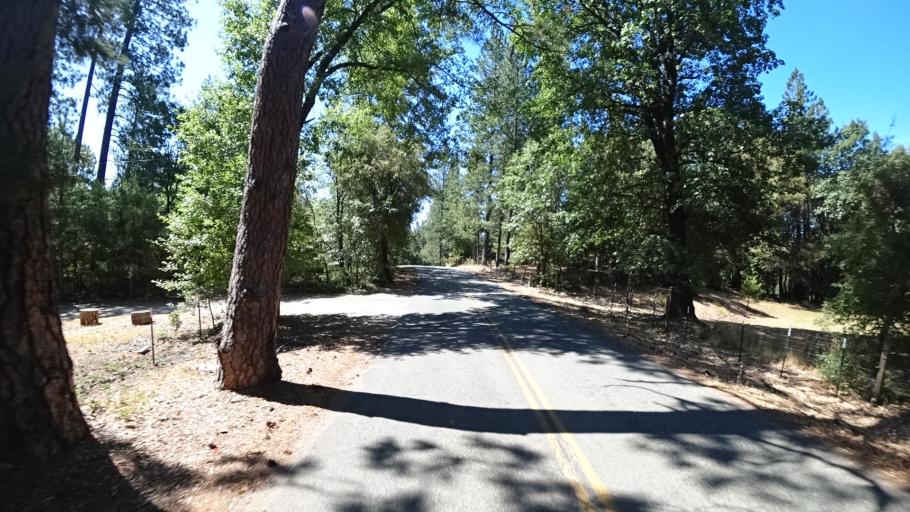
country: US
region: California
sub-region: Amador County
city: Pioneer
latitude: 38.4028
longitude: -120.5059
